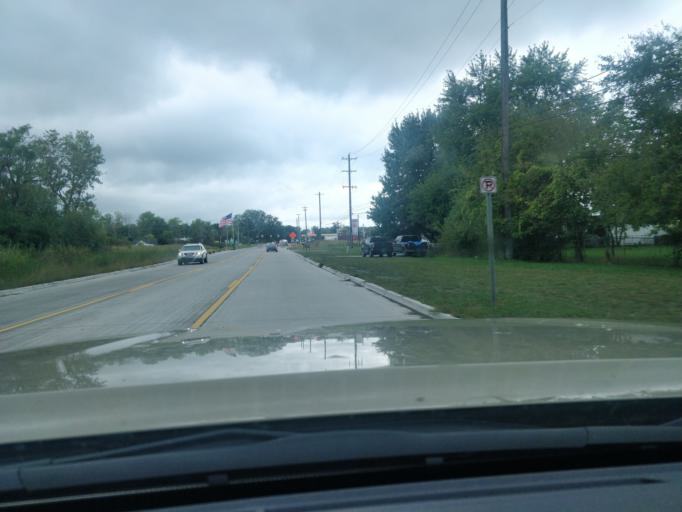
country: US
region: Michigan
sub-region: Wayne County
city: Woodhaven
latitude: 42.1677
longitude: -83.2627
